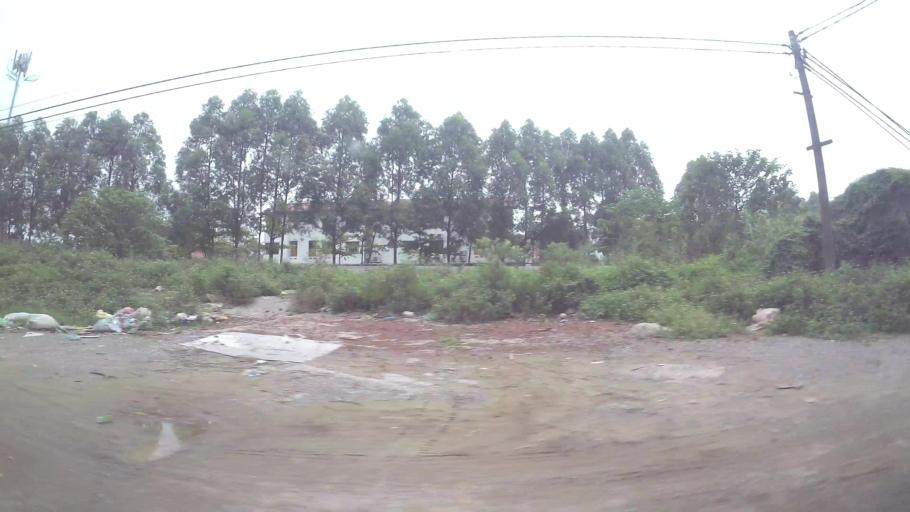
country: VN
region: Ha Noi
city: Van Dien
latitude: 20.9767
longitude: 105.8777
